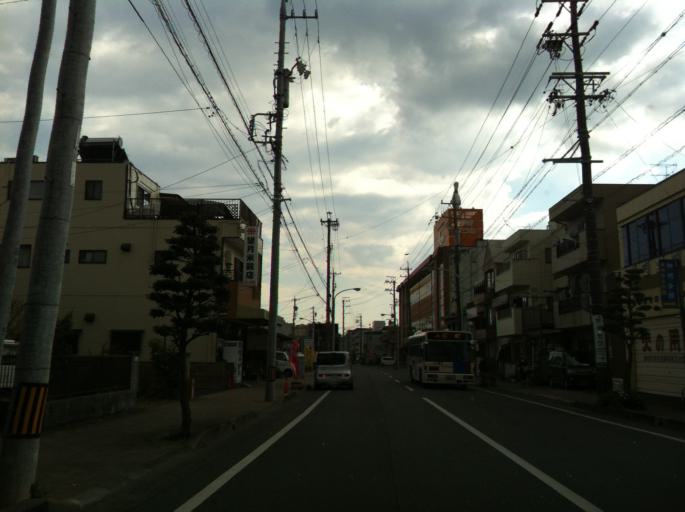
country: JP
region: Shizuoka
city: Shizuoka-shi
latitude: 34.9835
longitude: 138.3695
